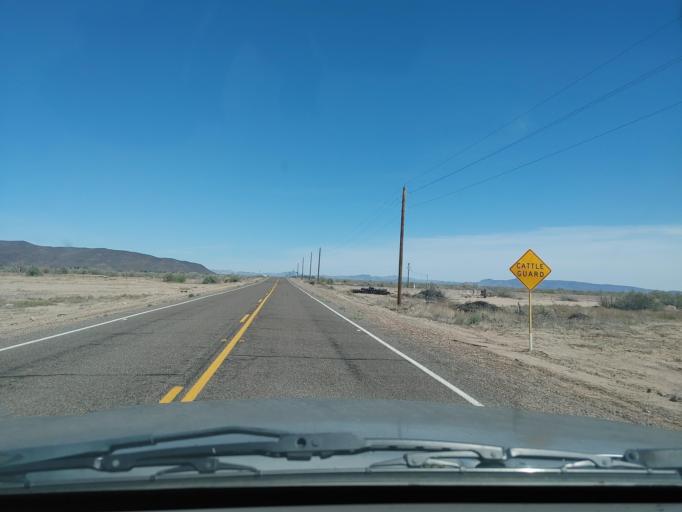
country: US
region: Arizona
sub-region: Maricopa County
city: Gila Bend
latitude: 32.9596
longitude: -113.3058
